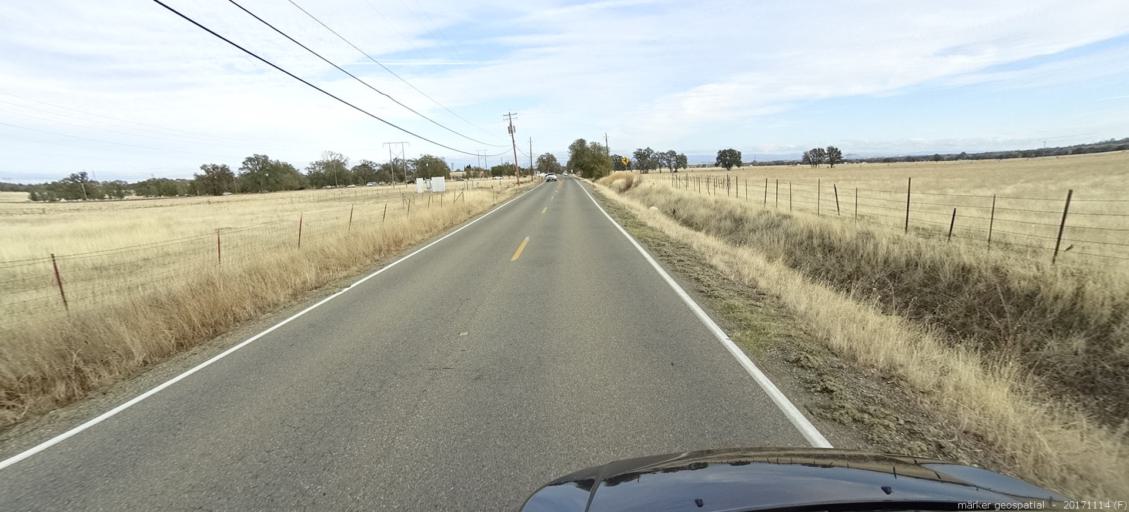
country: US
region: California
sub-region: Shasta County
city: Anderson
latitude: 40.3886
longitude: -122.4104
